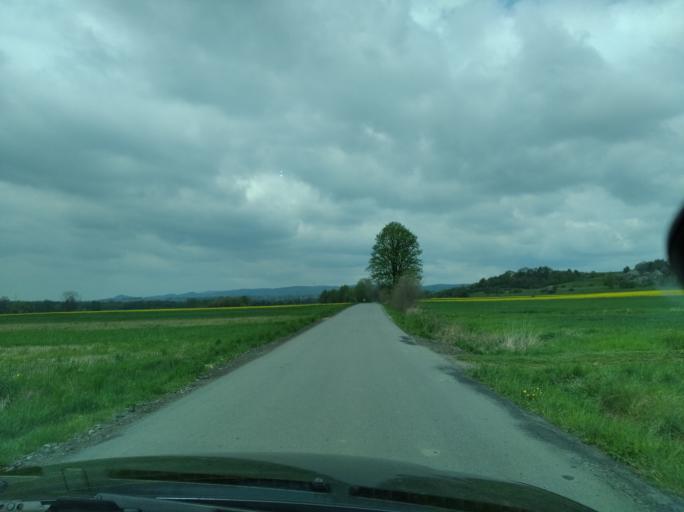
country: PL
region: Subcarpathian Voivodeship
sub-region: Powiat brzozowski
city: Jablonica Polska
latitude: 49.6821
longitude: 21.8981
